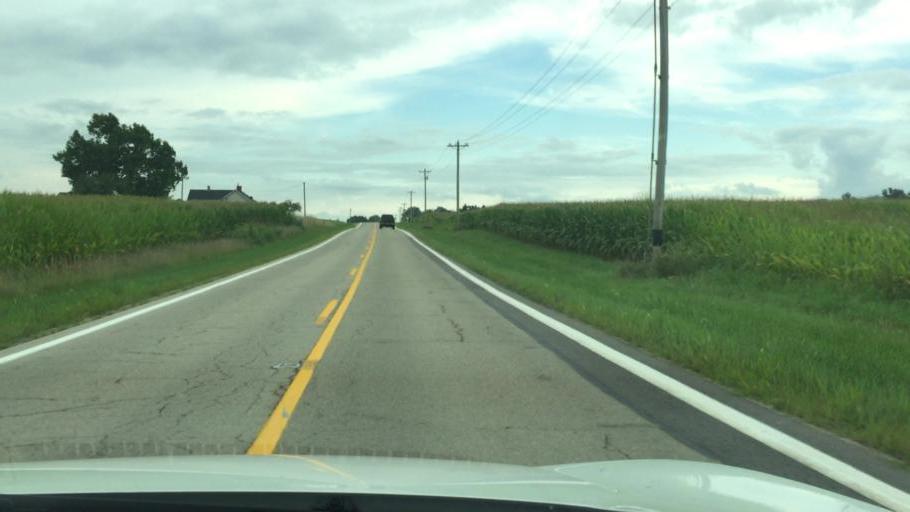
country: US
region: Ohio
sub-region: Champaign County
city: Mechanicsburg
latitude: 40.1117
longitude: -83.5226
